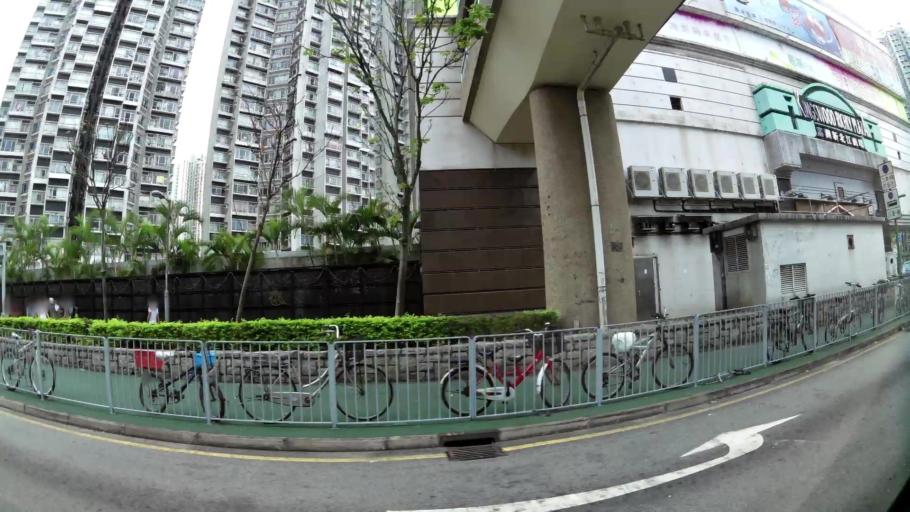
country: HK
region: Yuen Long
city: Yuen Long Kau Hui
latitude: 22.4517
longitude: 114.0017
